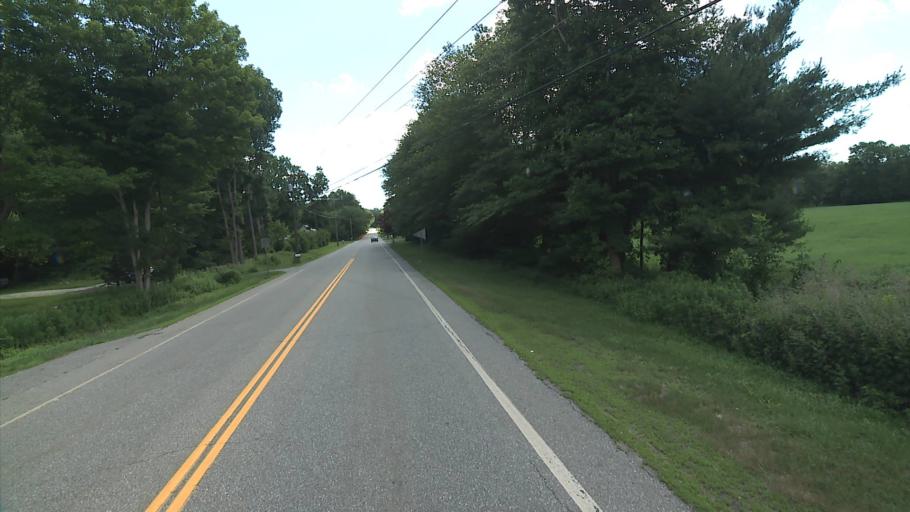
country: US
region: Connecticut
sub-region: New London County
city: Pawcatuck
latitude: 41.4221
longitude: -71.8786
